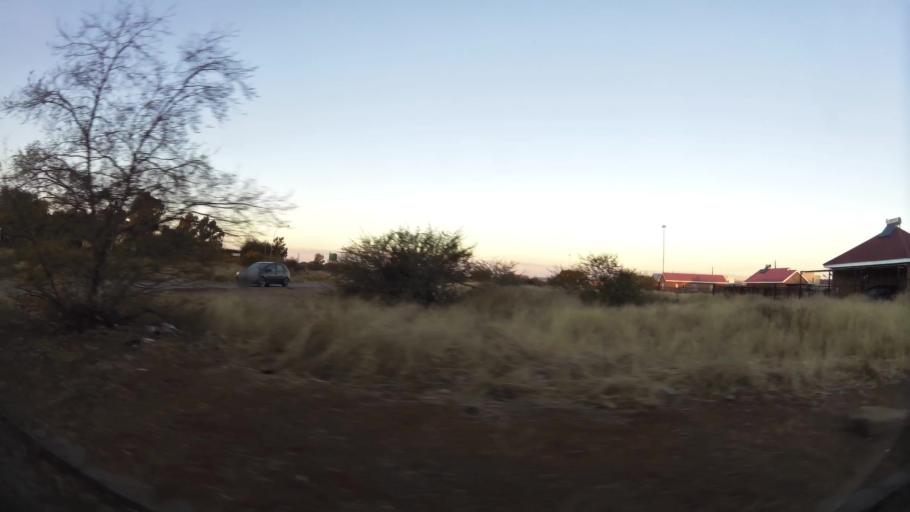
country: ZA
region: Northern Cape
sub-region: Frances Baard District Municipality
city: Kimberley
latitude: -28.7309
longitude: 24.7762
